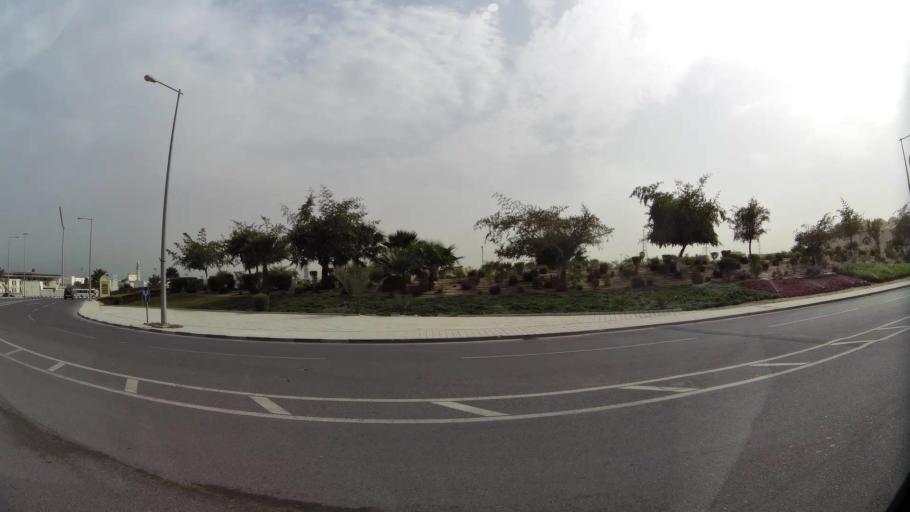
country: QA
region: Baladiyat ad Dawhah
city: Doha
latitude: 25.3189
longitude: 51.5088
